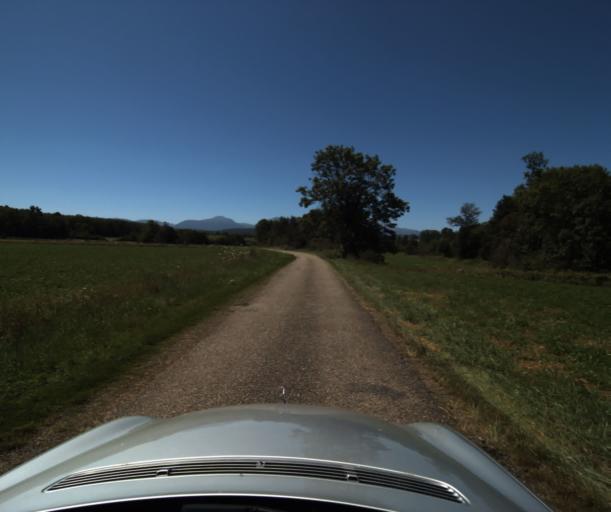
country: FR
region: Languedoc-Roussillon
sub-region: Departement de l'Aude
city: Chalabre
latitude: 42.9954
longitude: 1.9263
